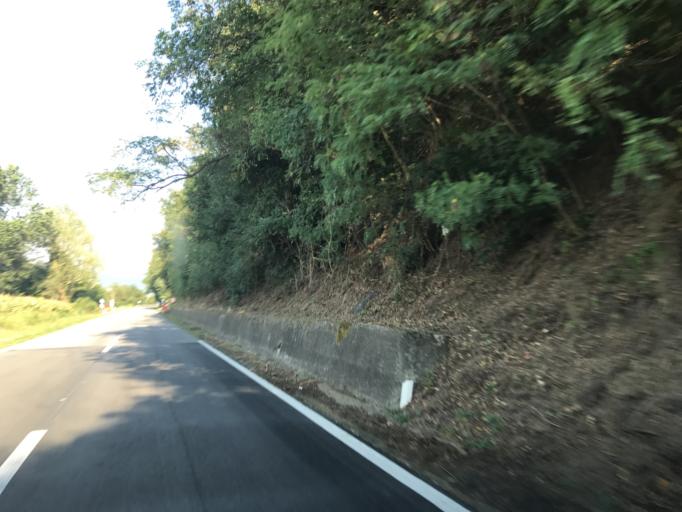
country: RO
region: Caras-Severin
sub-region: Comuna Berzasca
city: Liubcova
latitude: 44.6464
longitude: 21.8646
